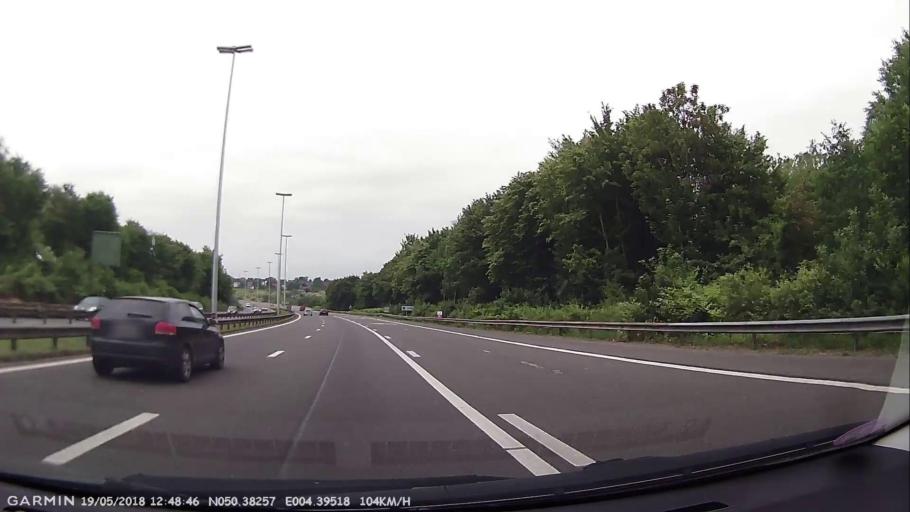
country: BE
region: Wallonia
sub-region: Province du Hainaut
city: Charleroi
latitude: 50.3827
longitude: 4.3945
